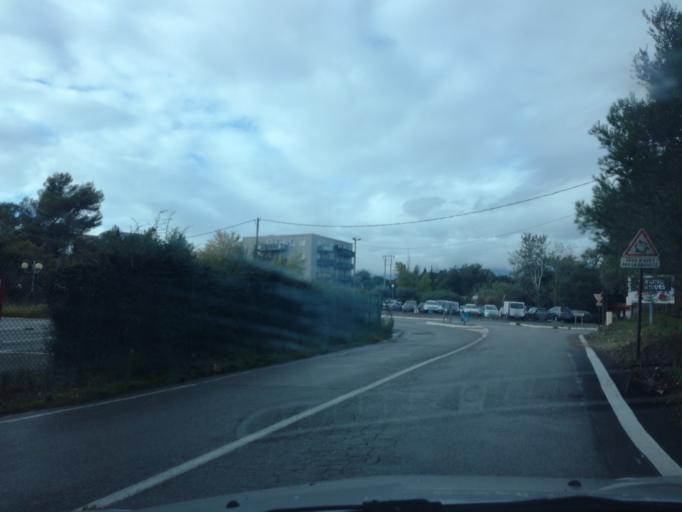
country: FR
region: Provence-Alpes-Cote d'Azur
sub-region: Departement des Alpes-Maritimes
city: Pegomas
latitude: 43.6195
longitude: 6.9333
